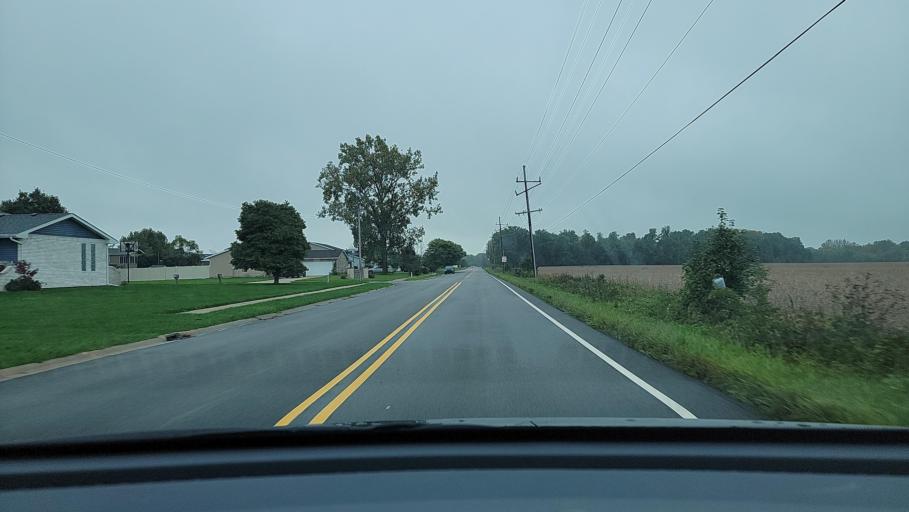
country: US
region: Indiana
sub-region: Porter County
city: Portage
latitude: 41.5444
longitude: -87.1970
